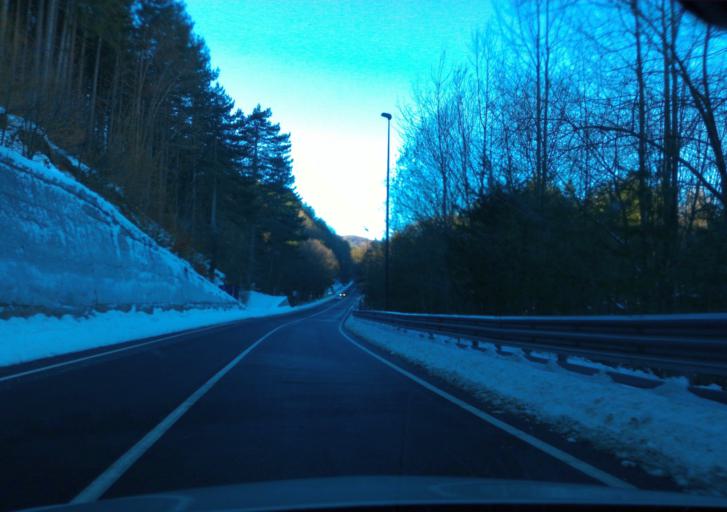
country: IT
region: Calabria
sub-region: Provincia di Cosenza
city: Celico
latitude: 39.3387
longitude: 16.4483
